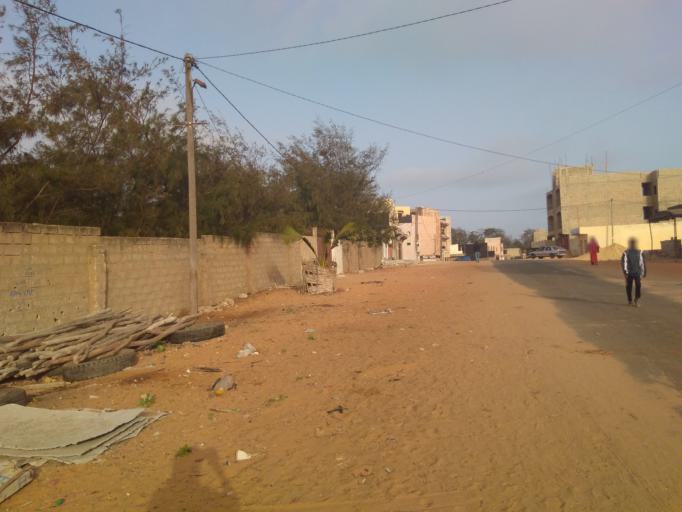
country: SN
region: Dakar
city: Pikine
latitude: 14.8021
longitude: -17.3397
